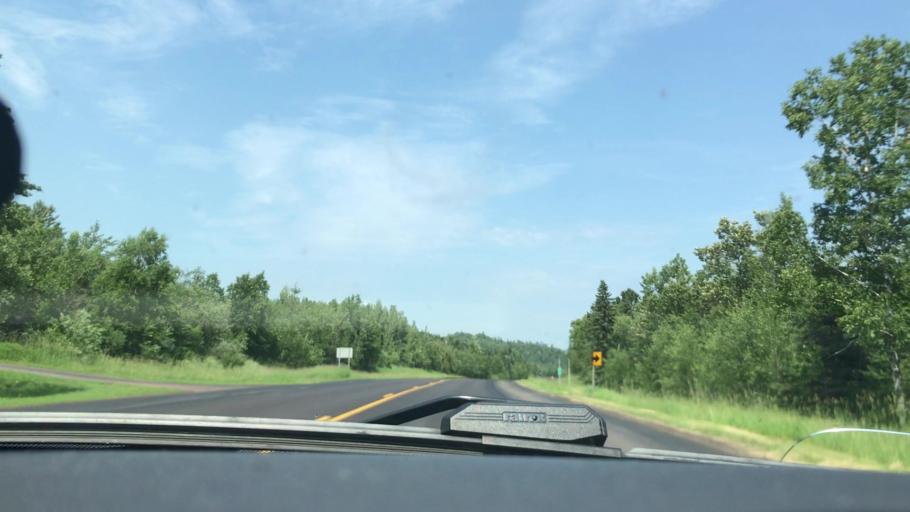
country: US
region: Minnesota
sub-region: Lake County
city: Silver Bay
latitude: 47.3549
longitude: -91.1811
